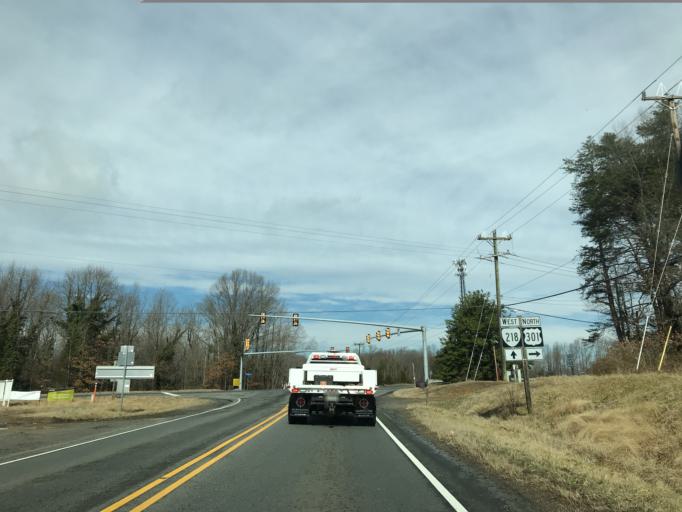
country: US
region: Virginia
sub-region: King George County
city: Dahlgren
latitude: 38.3348
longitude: -77.0839
